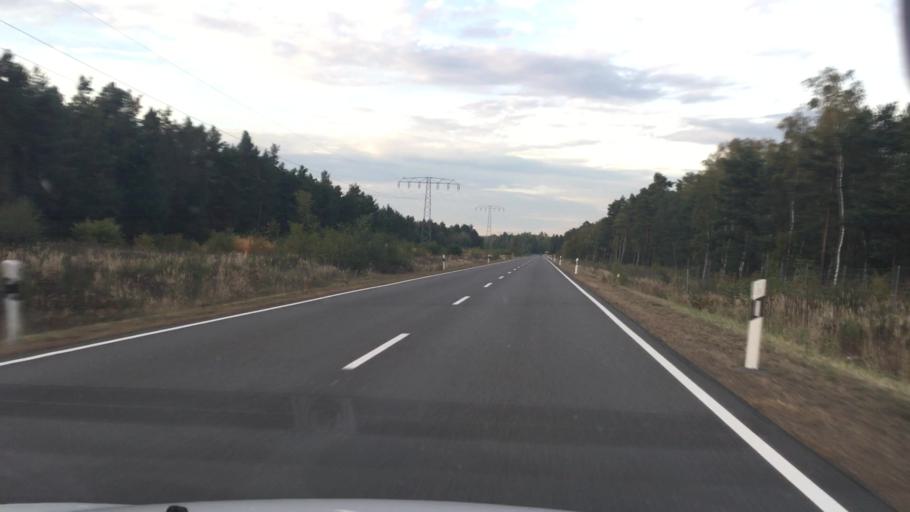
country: DE
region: Brandenburg
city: Schipkau
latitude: 51.5126
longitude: 13.9086
